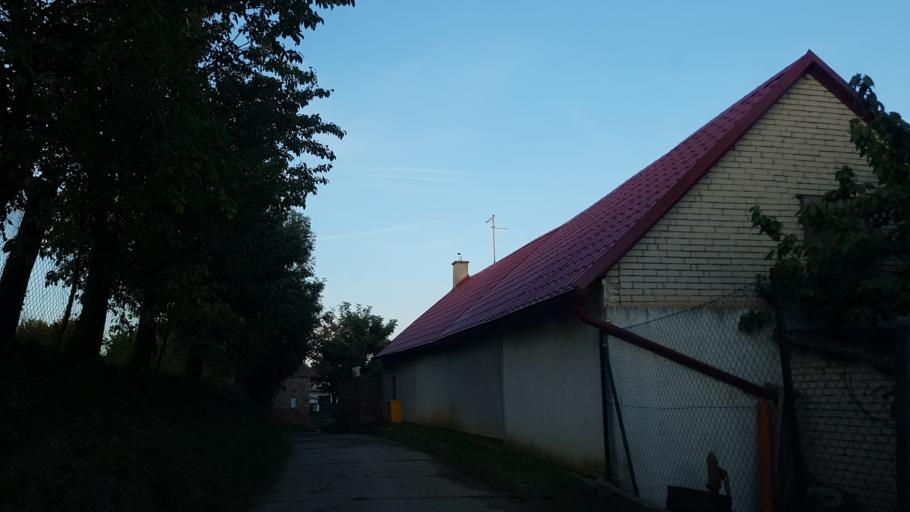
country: CZ
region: Zlin
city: Polesovice
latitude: 49.0303
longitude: 17.3382
